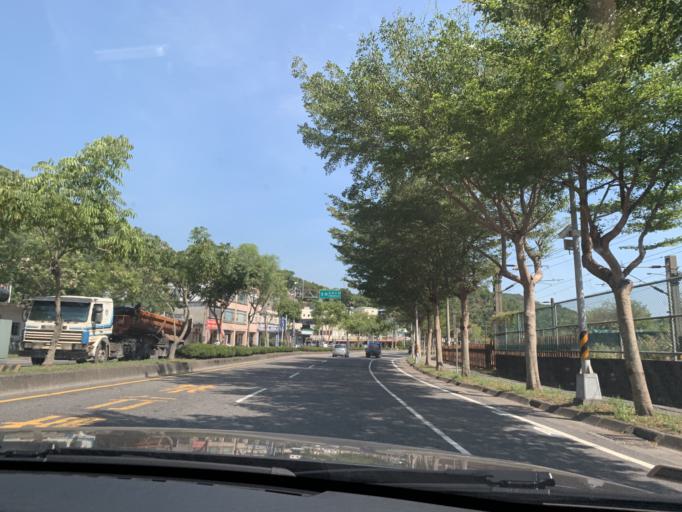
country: TW
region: Taiwan
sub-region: Yilan
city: Yilan
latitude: 24.5977
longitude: 121.8347
